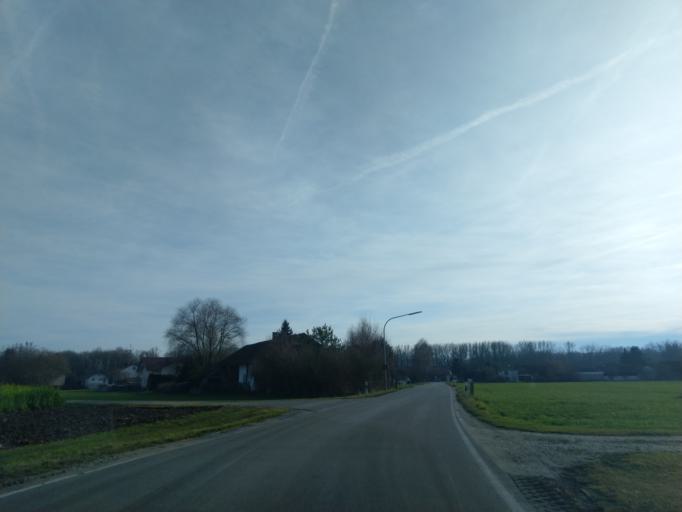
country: DE
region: Bavaria
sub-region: Lower Bavaria
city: Oberporing
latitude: 48.7107
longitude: 12.8151
